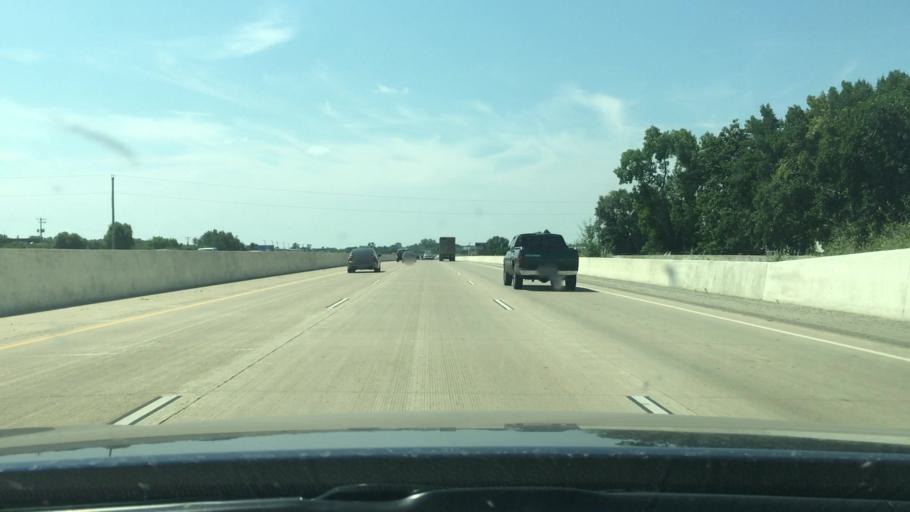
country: US
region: Wisconsin
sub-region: Winnebago County
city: Neenah
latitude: 44.1355
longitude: -88.4945
